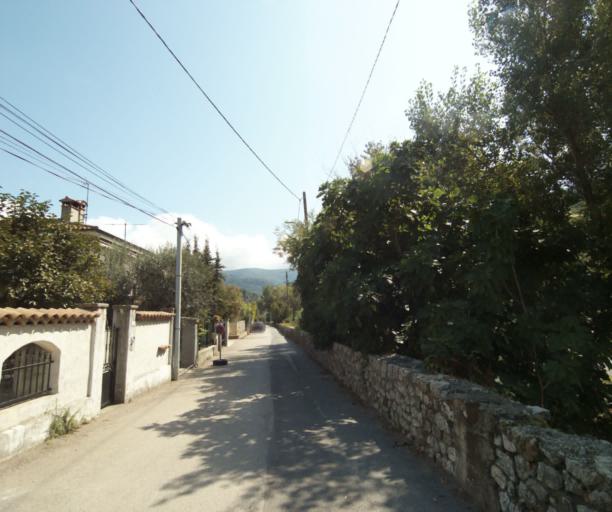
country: FR
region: Provence-Alpes-Cote d'Azur
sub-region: Departement des Alpes-Maritimes
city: Cantaron
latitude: 43.7587
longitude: 7.3184
